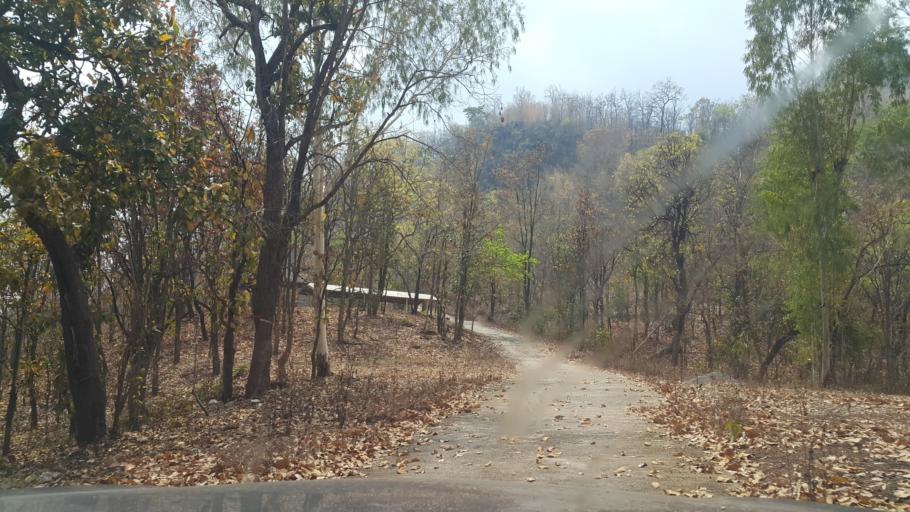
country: TH
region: Lamphun
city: Ban Hong
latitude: 18.2377
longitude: 98.8206
